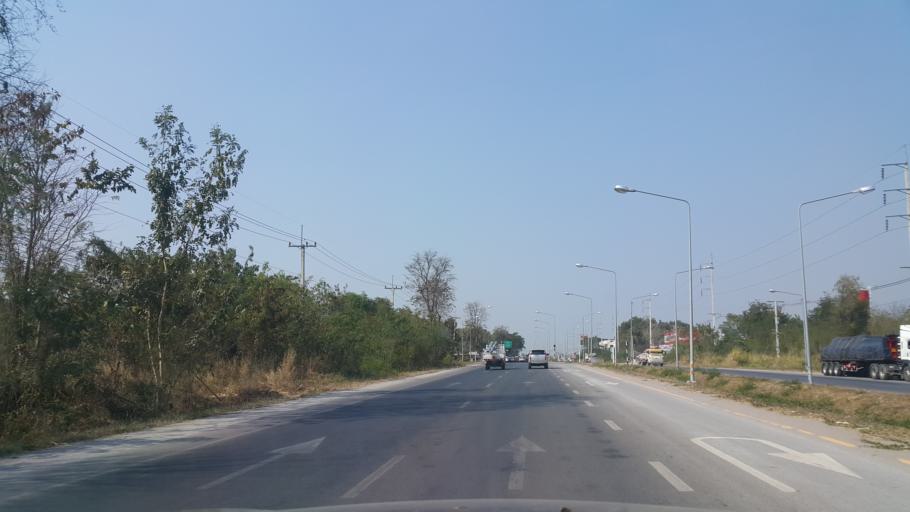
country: TH
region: Chaiyaphum
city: Phu Khiao
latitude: 16.4199
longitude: 102.1313
